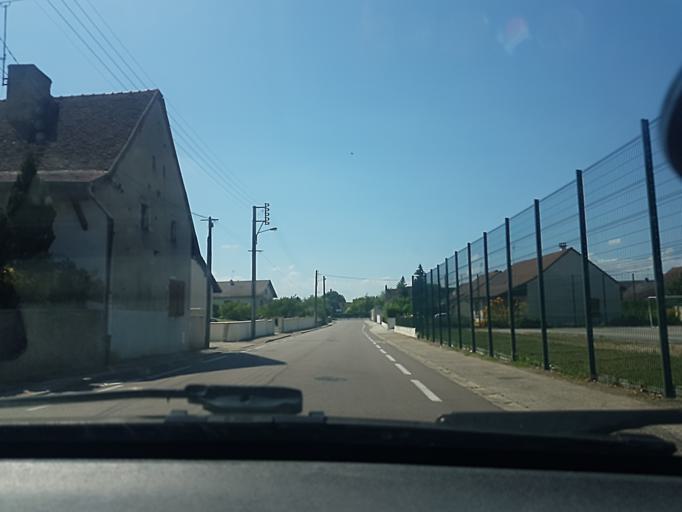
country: FR
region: Bourgogne
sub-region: Departement de Saone-et-Loire
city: Saint-Marcel
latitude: 46.7736
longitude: 4.8892
